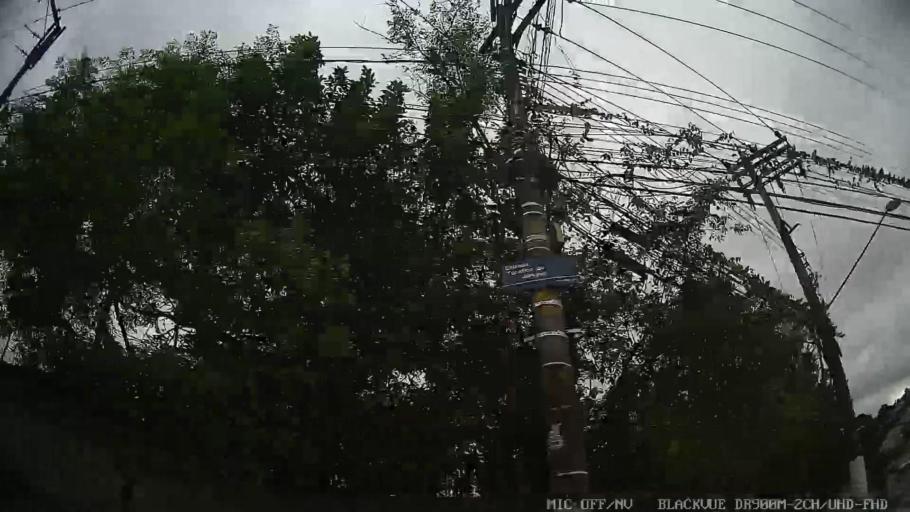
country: BR
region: Sao Paulo
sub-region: Osasco
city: Osasco
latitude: -23.4686
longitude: -46.7542
